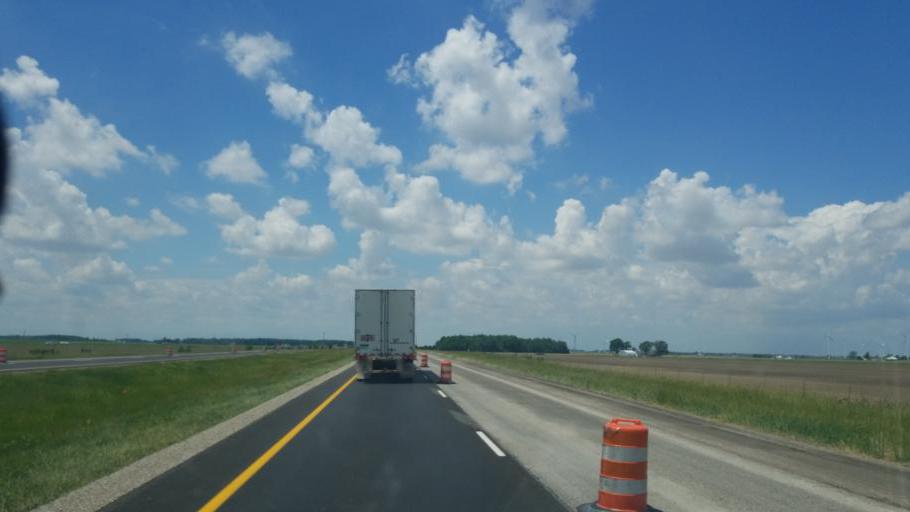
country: US
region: Ohio
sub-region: Van Wert County
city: Convoy
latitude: 40.9618
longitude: -84.7401
